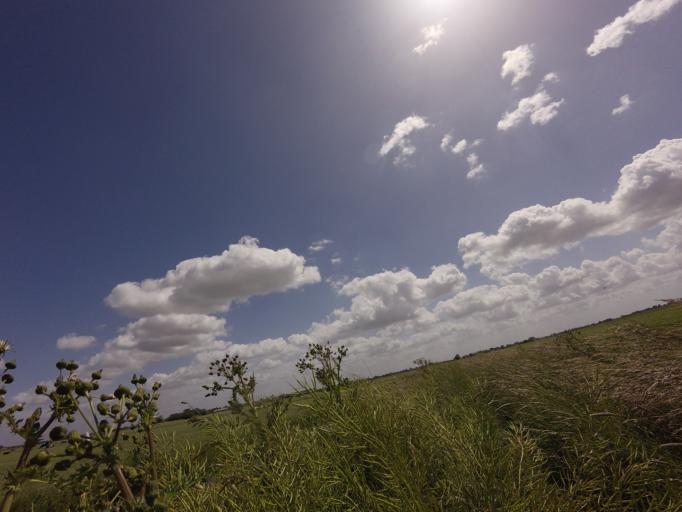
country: NL
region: Utrecht
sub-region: Gemeente Montfoort
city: Montfoort
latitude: 52.0503
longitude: 4.9100
